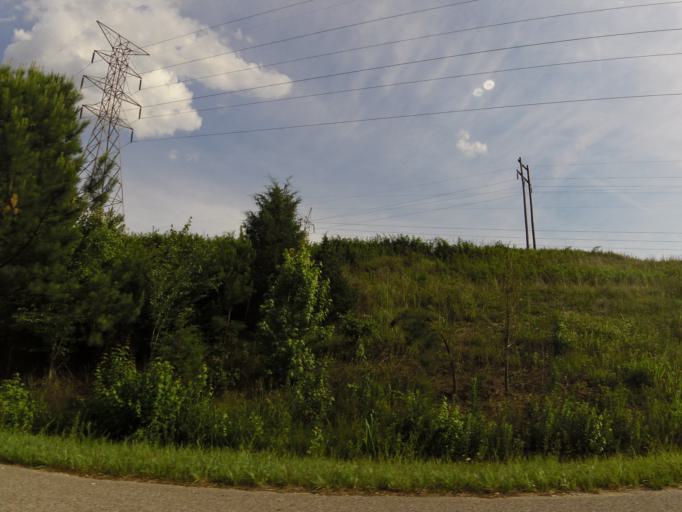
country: US
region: Tennessee
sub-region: Benton County
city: Camden
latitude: 36.0267
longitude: -88.0878
